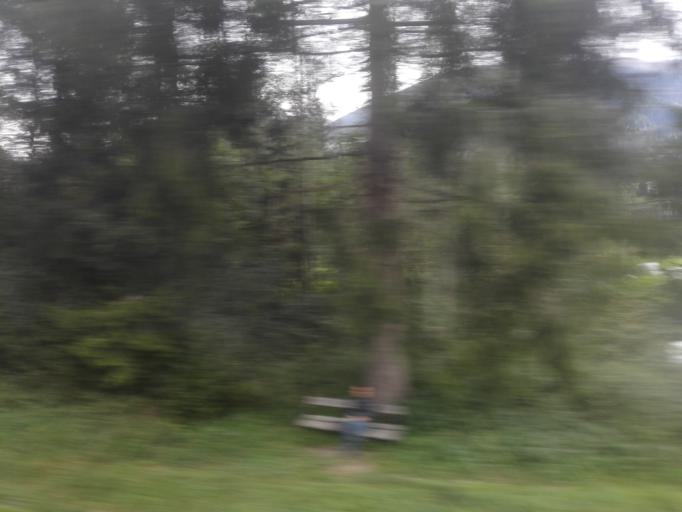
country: AT
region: Salzburg
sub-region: Politischer Bezirk Zell am See
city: Neukirchen am Grossvenediger
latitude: 47.2455
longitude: 12.2752
